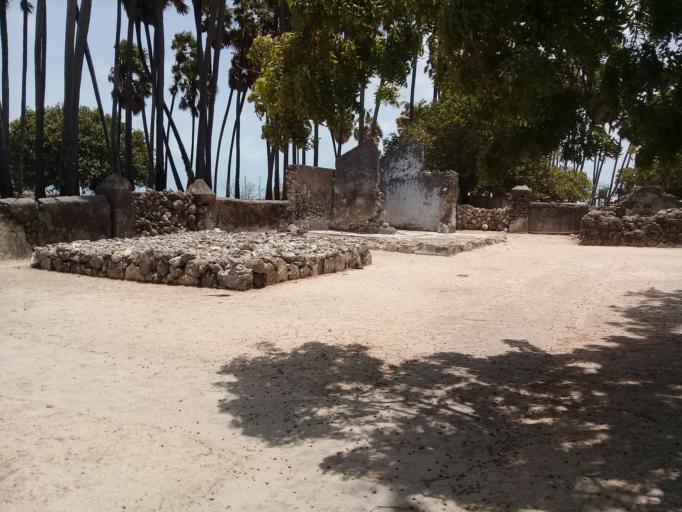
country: LK
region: Northern Province
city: Jaffna
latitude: 9.5275
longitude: 79.7027
